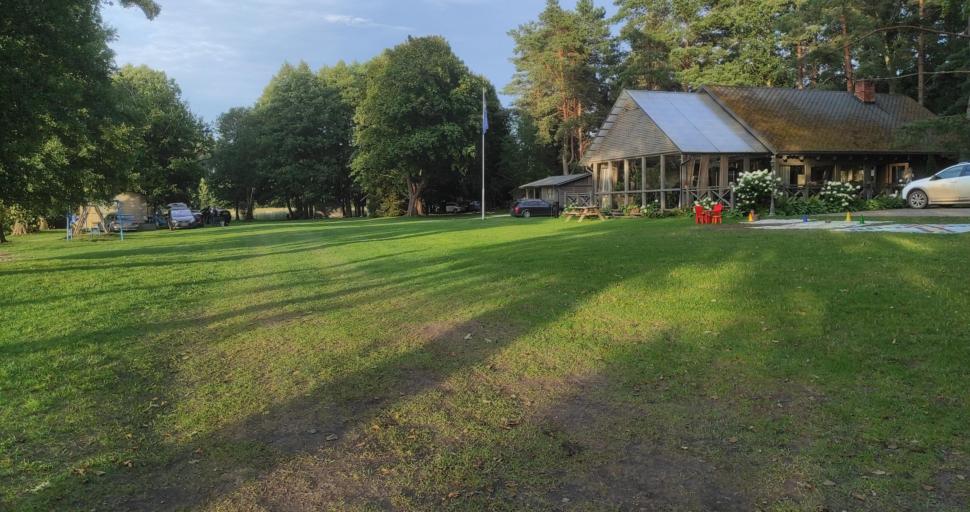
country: LV
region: Kuldigas Rajons
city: Kuldiga
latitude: 57.1230
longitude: 22.1890
